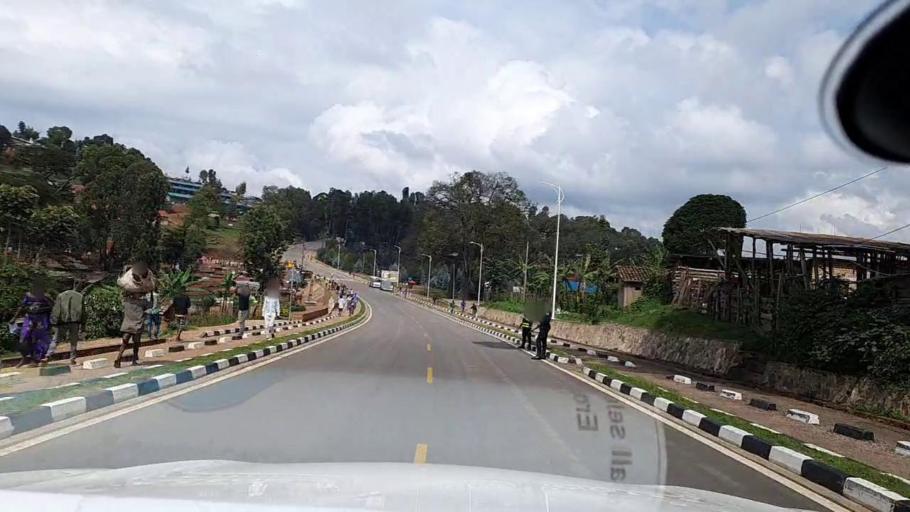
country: RW
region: Southern Province
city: Nzega
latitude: -2.4845
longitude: 29.5278
